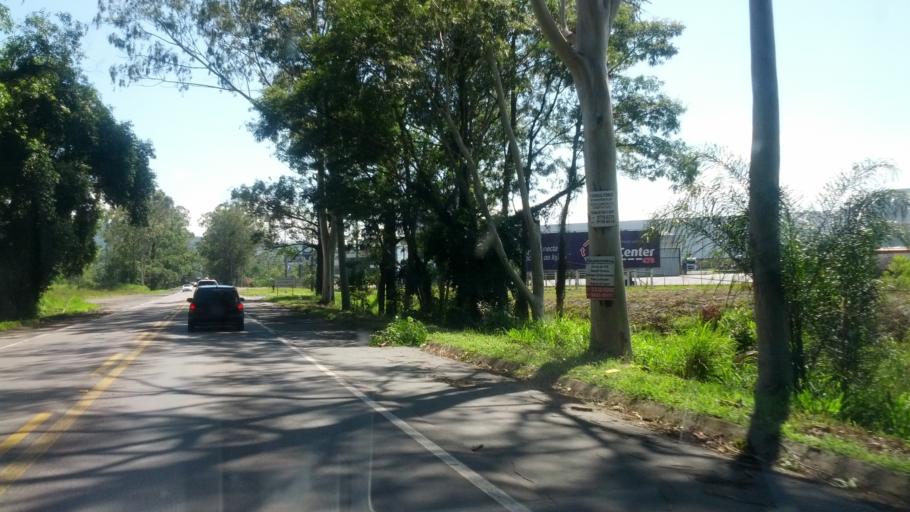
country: BR
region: Santa Catarina
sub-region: Rio Do Sul
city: Rio do Sul
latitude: -27.1790
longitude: -49.5959
